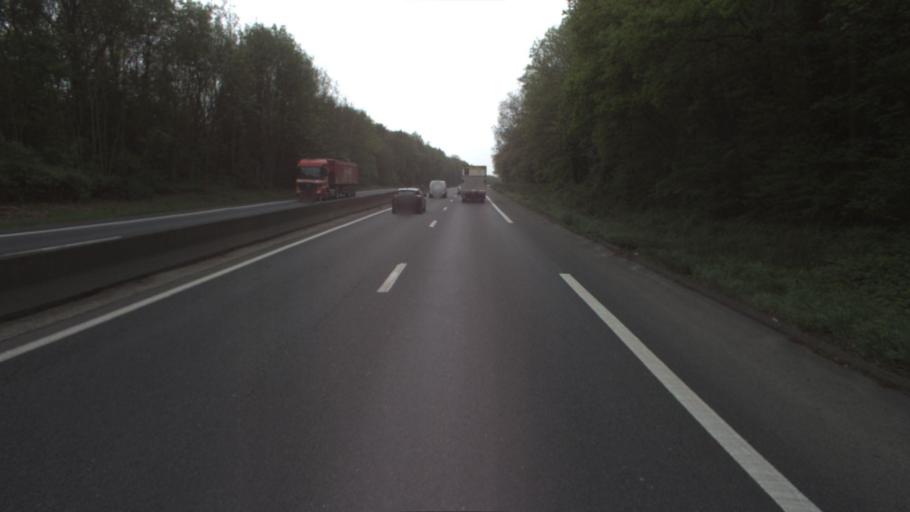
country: FR
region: Ile-de-France
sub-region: Departement de Seine-et-Marne
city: Saint-Mard
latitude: 49.0502
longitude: 2.6963
